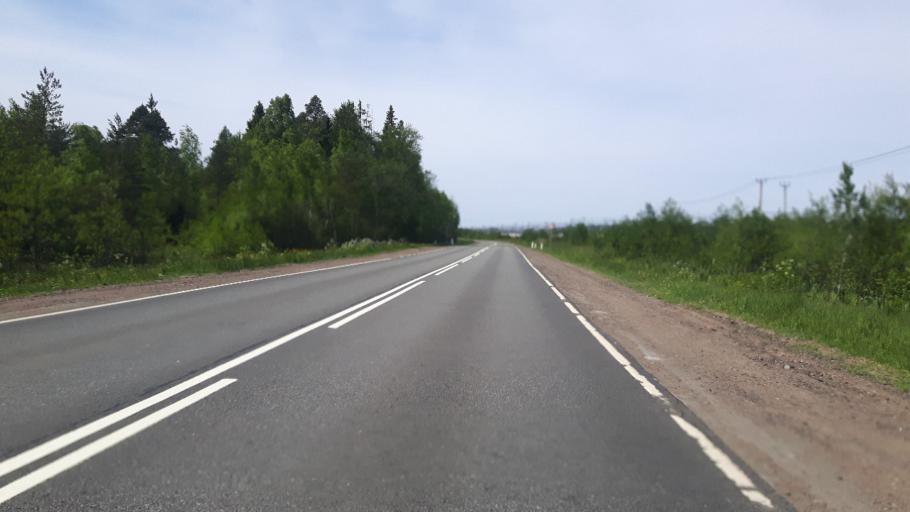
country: RU
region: Leningrad
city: Ust'-Luga
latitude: 59.6586
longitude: 28.4030
